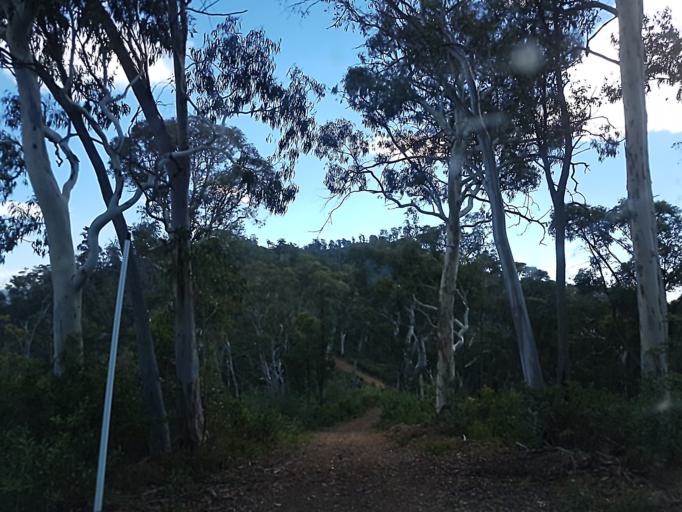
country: AU
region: Victoria
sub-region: Alpine
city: Mount Beauty
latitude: -36.9111
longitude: 147.0152
